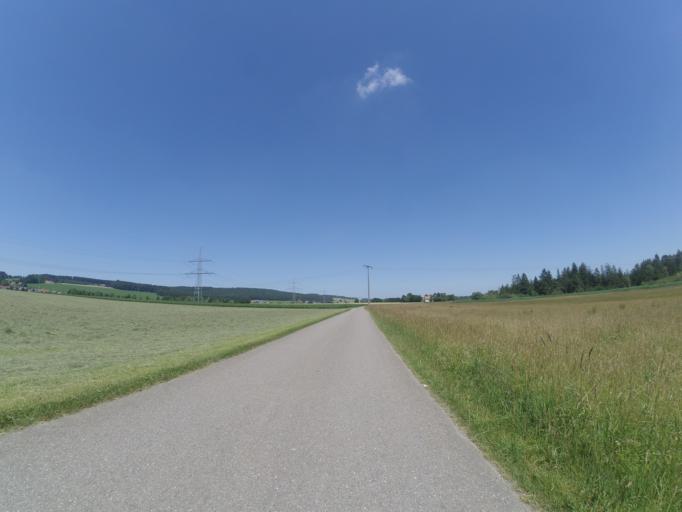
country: DE
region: Baden-Wuerttemberg
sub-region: Tuebingen Region
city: Bad Wurzach
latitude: 47.8993
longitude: 9.8461
